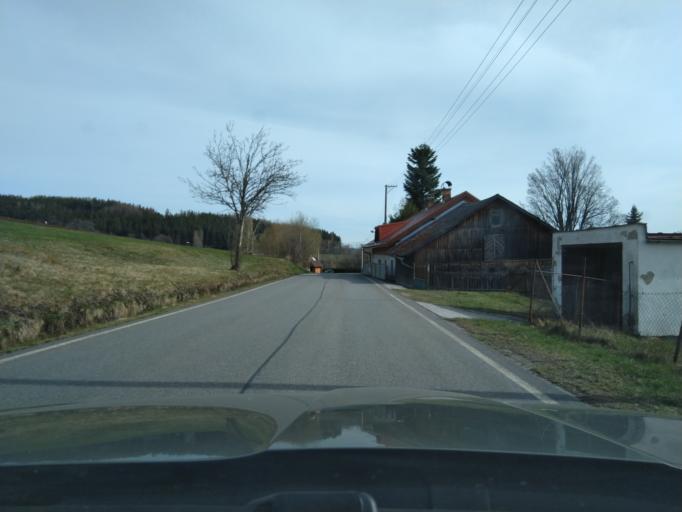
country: CZ
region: Jihocesky
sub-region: Okres Prachatice
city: Stachy
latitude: 49.0848
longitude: 13.6412
